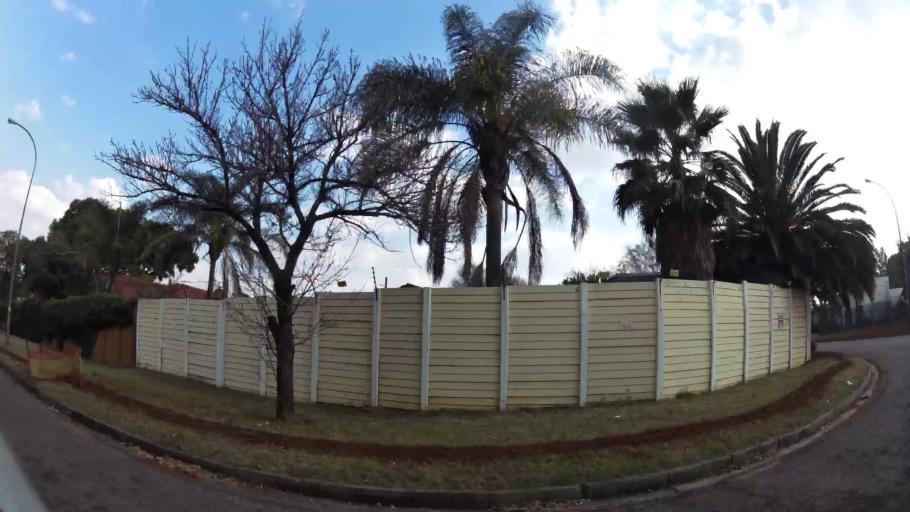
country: ZA
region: Gauteng
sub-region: Ekurhuleni Metropolitan Municipality
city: Germiston
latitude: -26.2495
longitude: 28.1780
